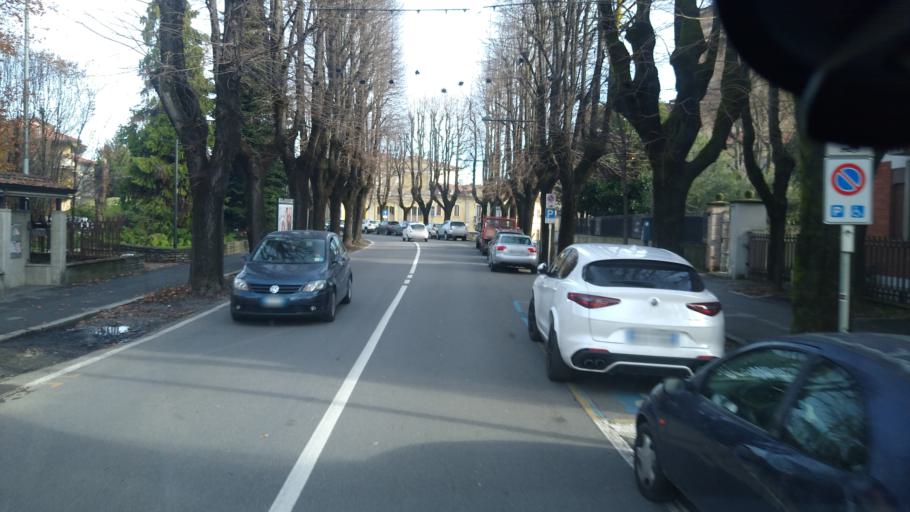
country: IT
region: Lombardy
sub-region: Provincia di Bergamo
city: Treviglio
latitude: 45.5217
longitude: 9.5896
